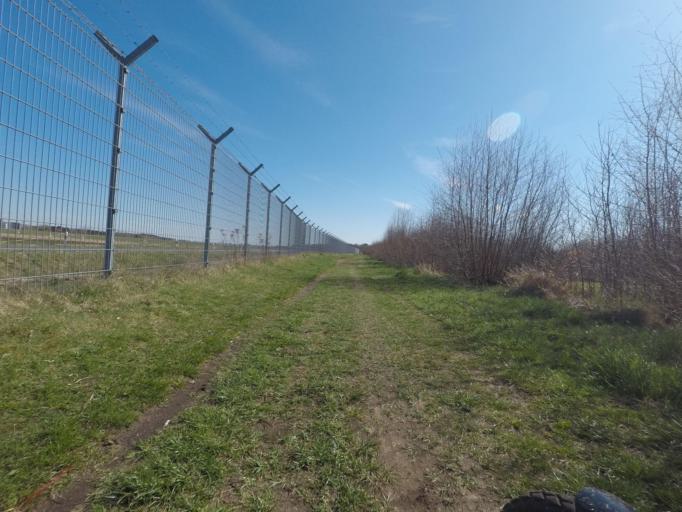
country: DE
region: Schleswig-Holstein
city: Norderstedt
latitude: 53.6563
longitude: 9.9714
